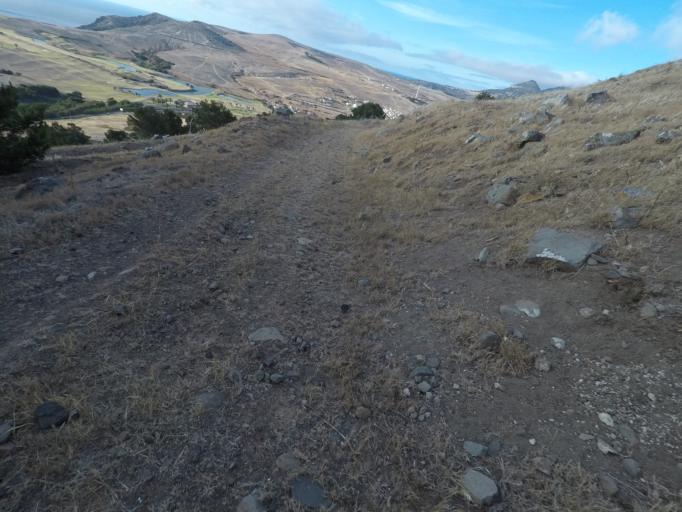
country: PT
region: Madeira
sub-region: Porto Santo
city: Vila de Porto Santo
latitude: 33.0462
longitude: -16.3699
